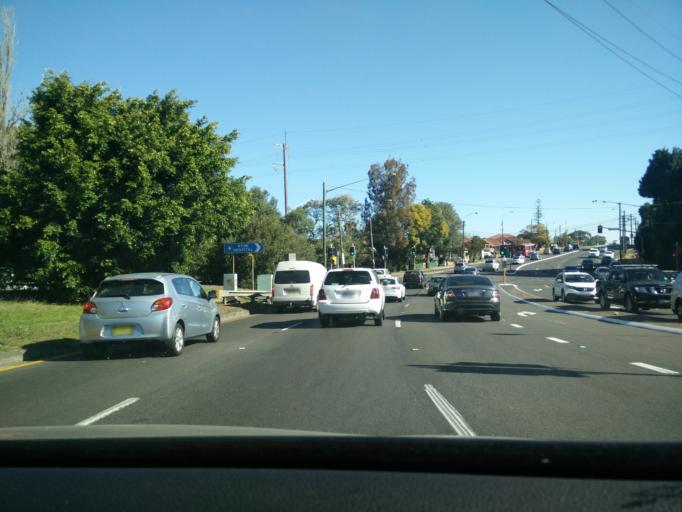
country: AU
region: New South Wales
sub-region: Ryde
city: North Ryde
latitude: -33.8033
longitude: 151.1137
